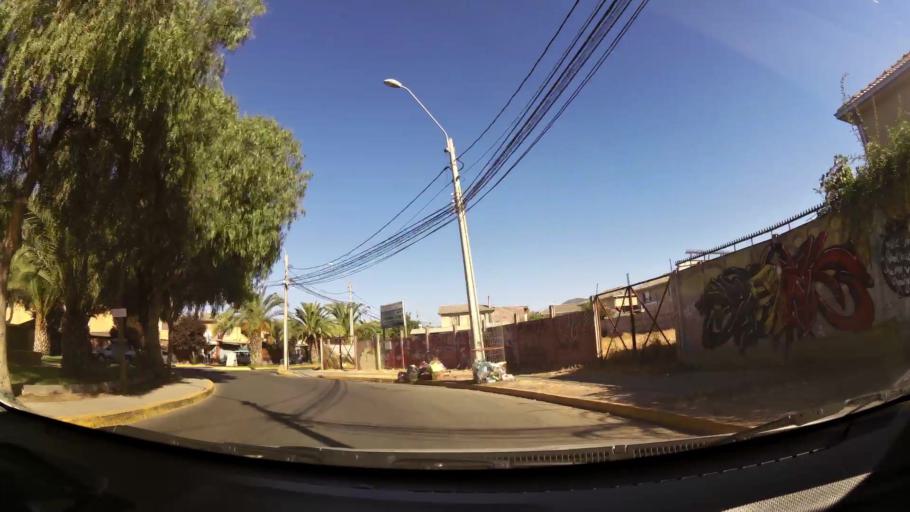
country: CL
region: O'Higgins
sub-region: Provincia de Cachapoal
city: Rancagua
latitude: -34.1798
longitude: -70.7575
